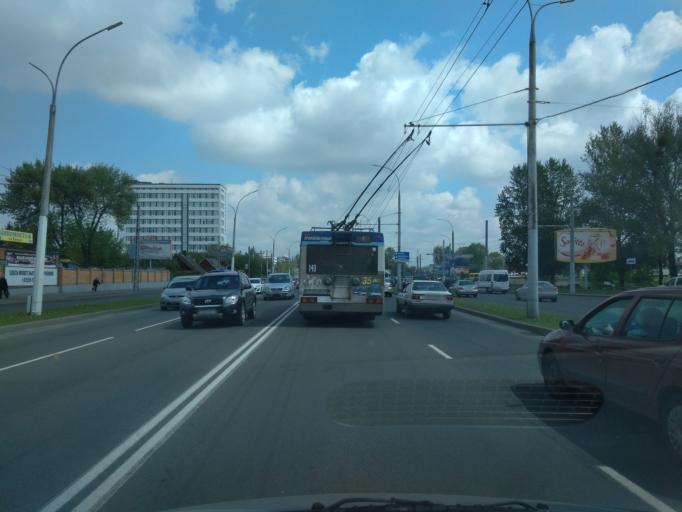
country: BY
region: Brest
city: Brest
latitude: 52.0928
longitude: 23.7291
